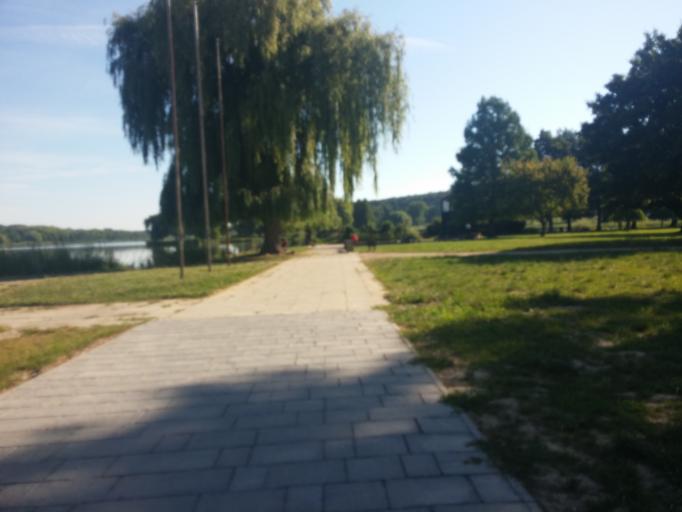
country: HU
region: Zala
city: Nagykanizsa
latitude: 46.4459
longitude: 17.0358
